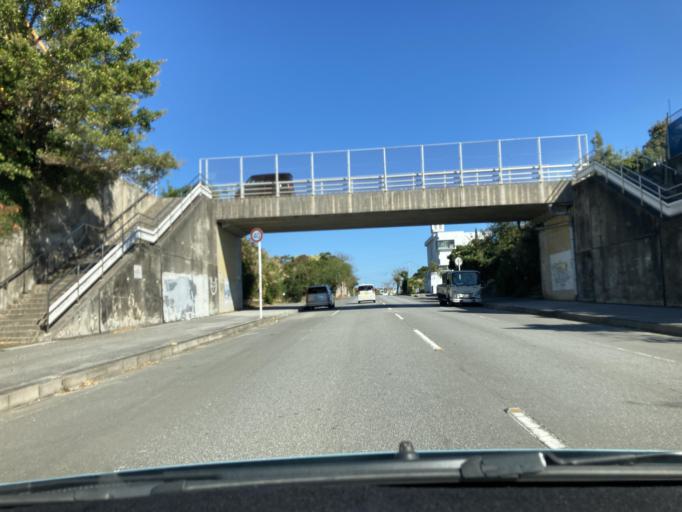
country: JP
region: Okinawa
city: Gushikawa
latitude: 26.3799
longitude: 127.8671
